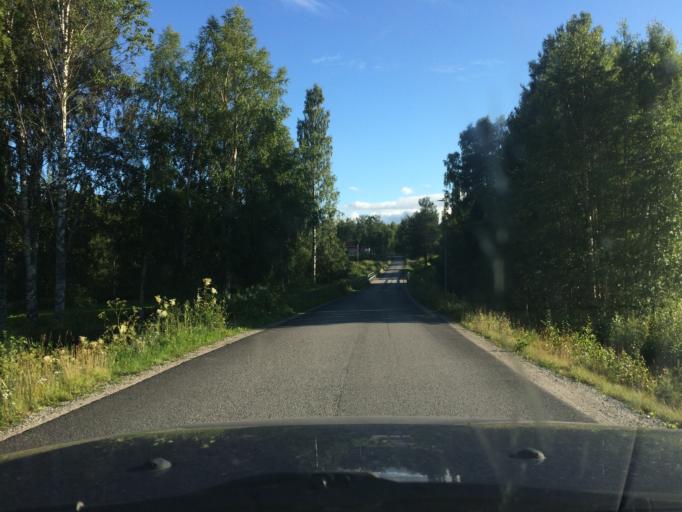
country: SE
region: Norrbotten
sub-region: Pitea Kommun
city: Roknas
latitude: 65.3465
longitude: 21.1812
